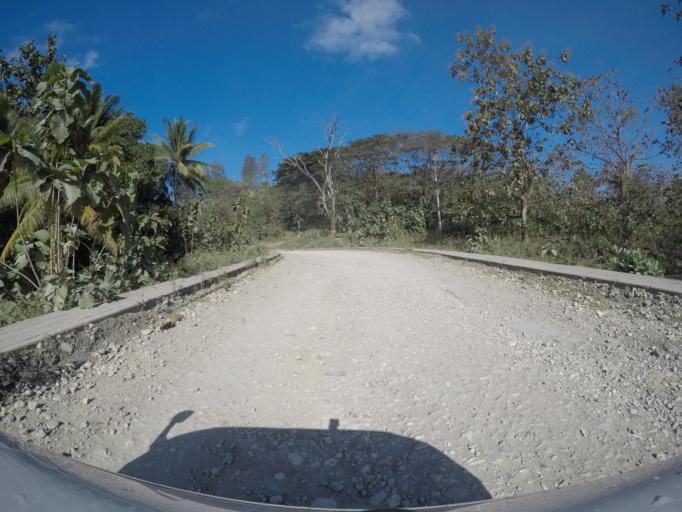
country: TL
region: Viqueque
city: Viqueque
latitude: -8.8452
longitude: 126.3697
